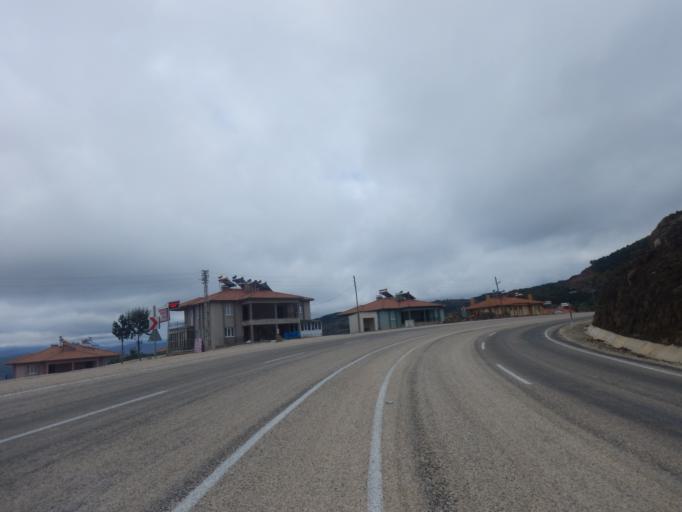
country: TR
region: Ordu
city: Mesudiye
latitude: 40.4330
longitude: 37.7762
